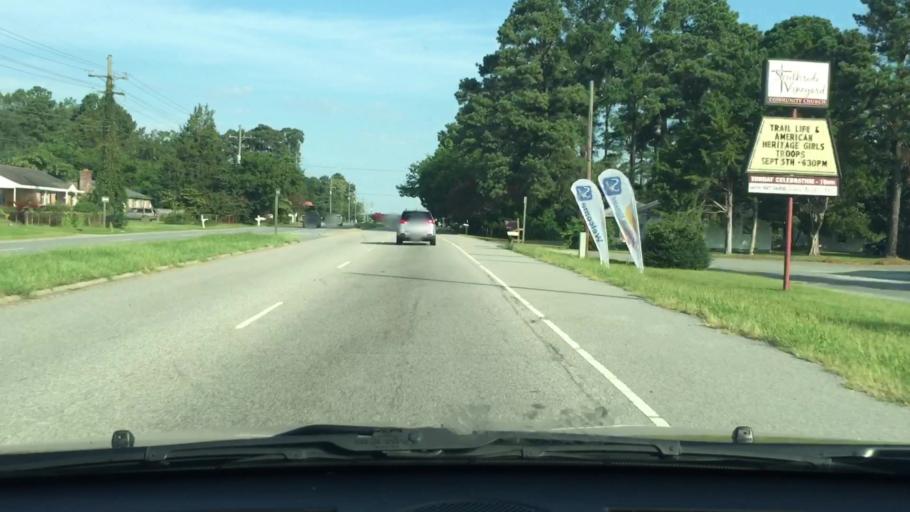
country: US
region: Virginia
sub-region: Isle of Wight County
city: Carrollton
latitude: 36.9422
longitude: -76.5894
